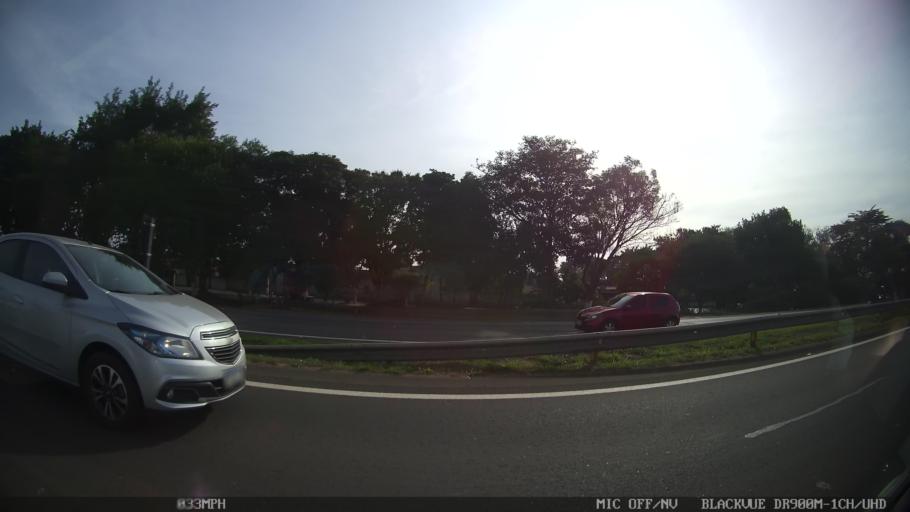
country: BR
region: Sao Paulo
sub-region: Piracicaba
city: Piracicaba
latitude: -22.6803
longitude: -47.7017
